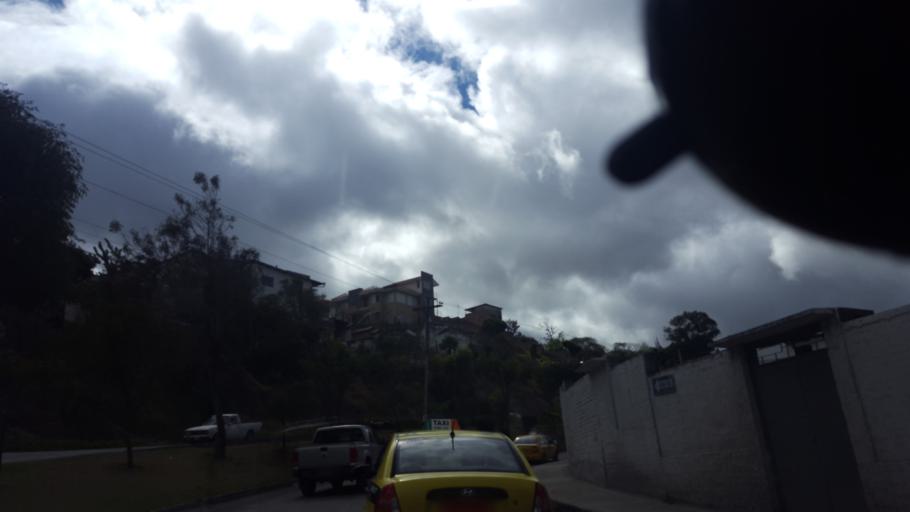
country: EC
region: Loja
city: Loja
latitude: -4.0015
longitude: -79.2075
